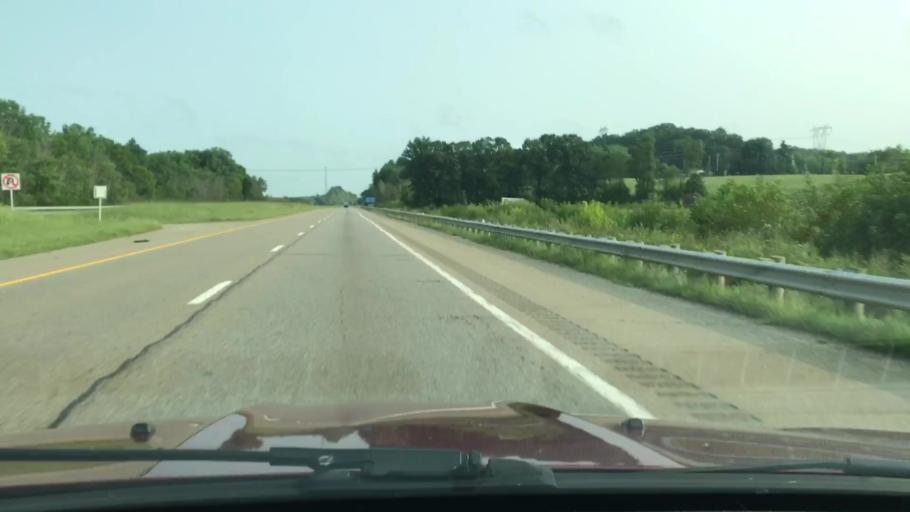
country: US
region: Ohio
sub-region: Guernsey County
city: Byesville
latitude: 39.9278
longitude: -81.5292
